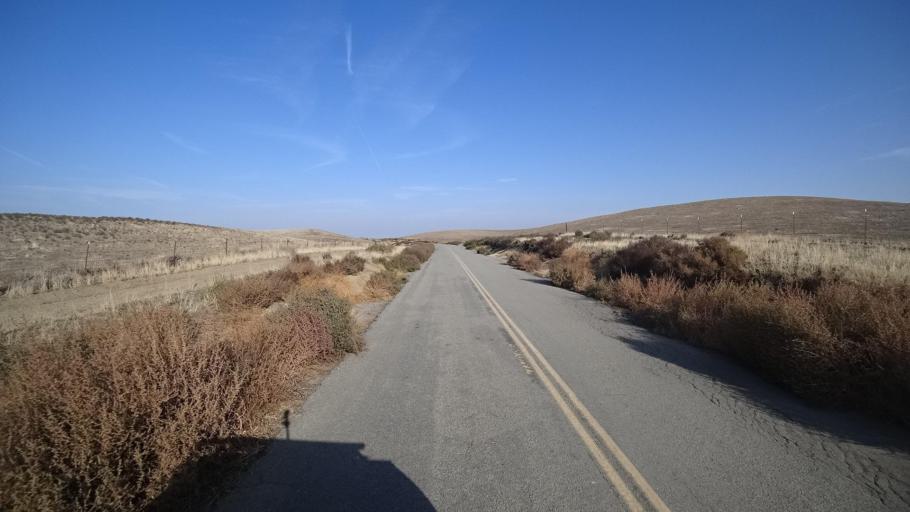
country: US
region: California
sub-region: Tulare County
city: Richgrove
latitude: 35.6258
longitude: -119.0306
